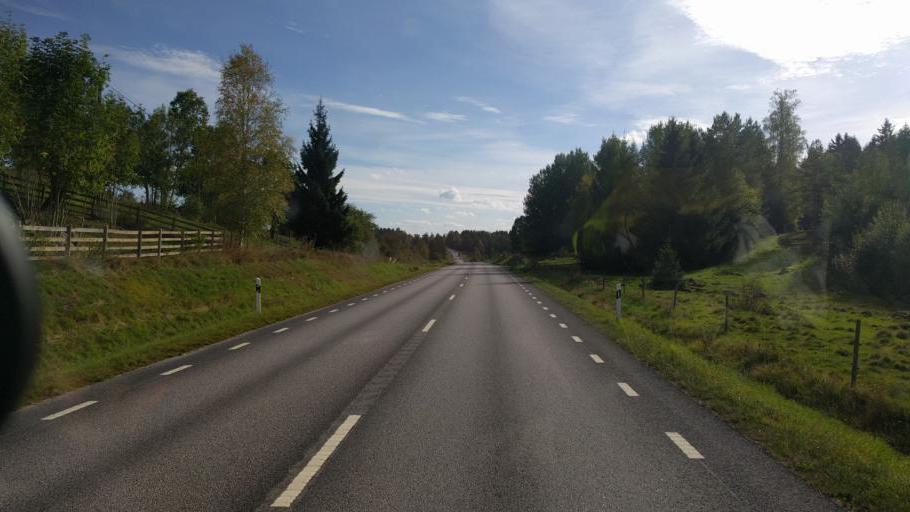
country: SE
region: OEstergoetland
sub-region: Kinda Kommun
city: Kisa
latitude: 57.9285
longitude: 15.6724
